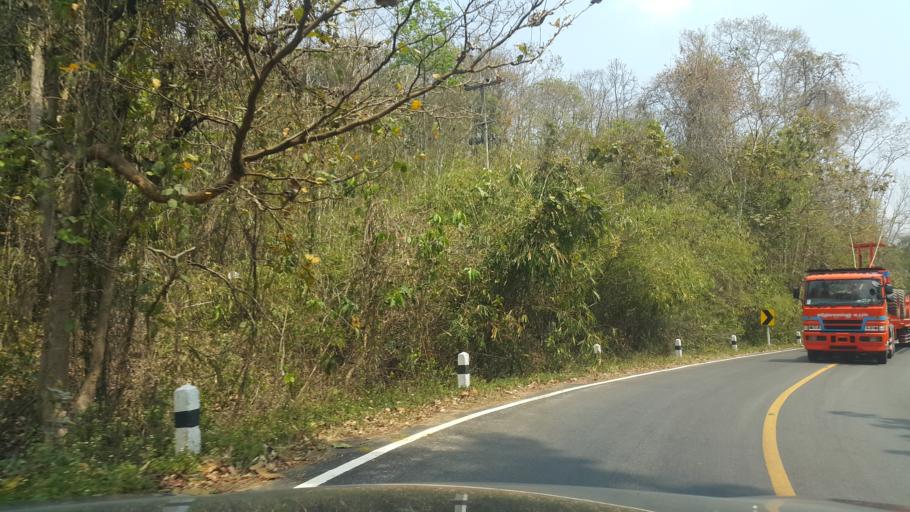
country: TH
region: Lamphun
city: Thung Hua Chang
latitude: 17.9062
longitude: 99.1190
